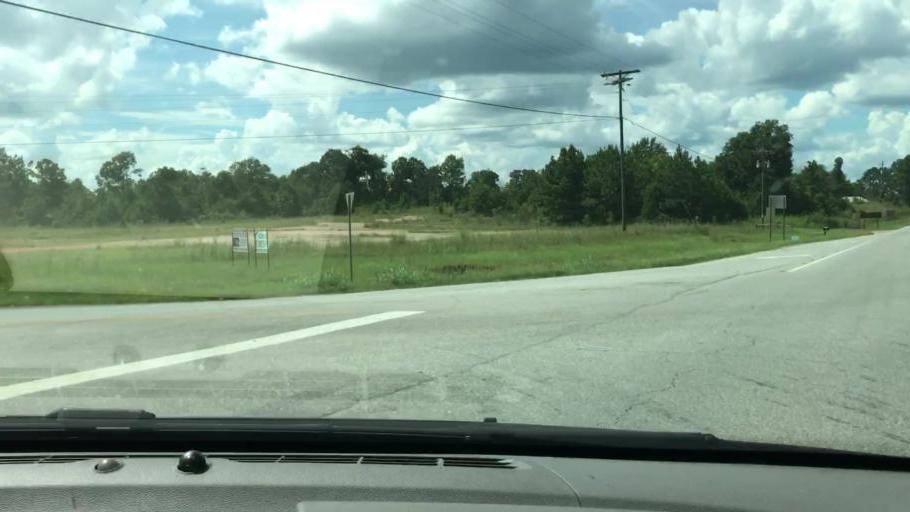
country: US
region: Georgia
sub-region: Quitman County
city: Georgetown
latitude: 31.8604
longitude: -85.0682
